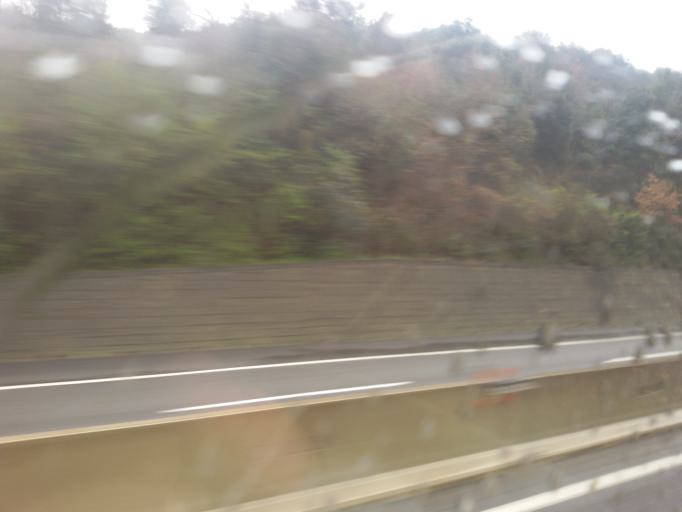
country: IT
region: Tuscany
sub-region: Province of Arezzo
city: Viciomaggio
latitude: 43.4535
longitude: 11.7551
